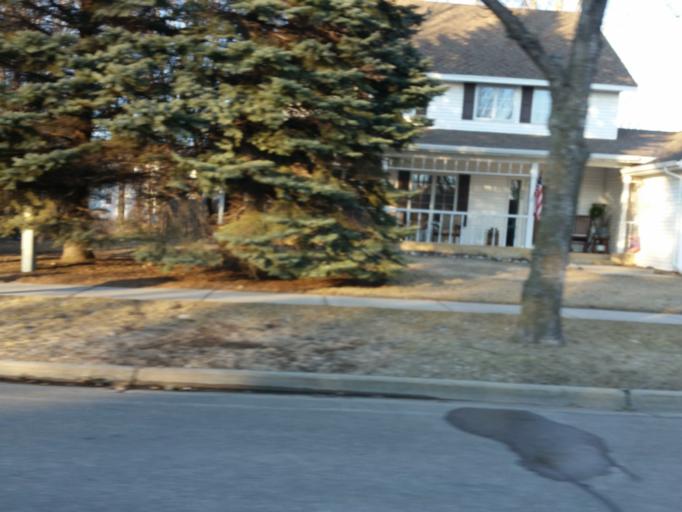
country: US
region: North Dakota
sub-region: Grand Forks County
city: Grand Forks
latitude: 47.8773
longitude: -97.0238
